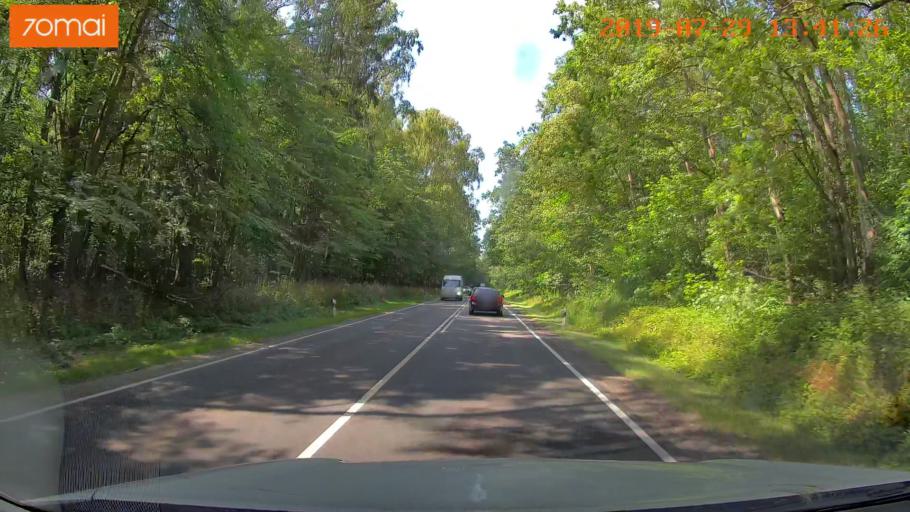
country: RU
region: Kaliningrad
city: Svetlyy
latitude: 54.7353
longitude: 20.1268
